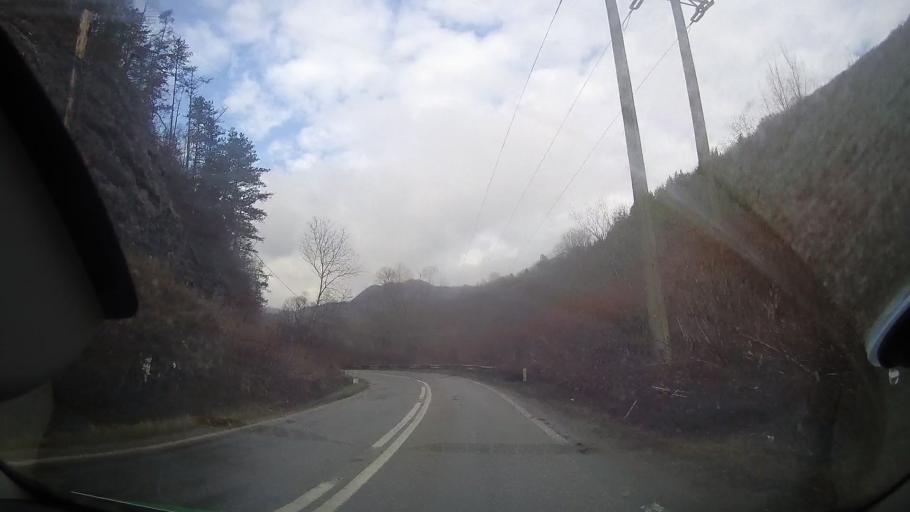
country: RO
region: Alba
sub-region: Comuna Ocolis
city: Ocolis
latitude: 46.4300
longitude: 23.4627
